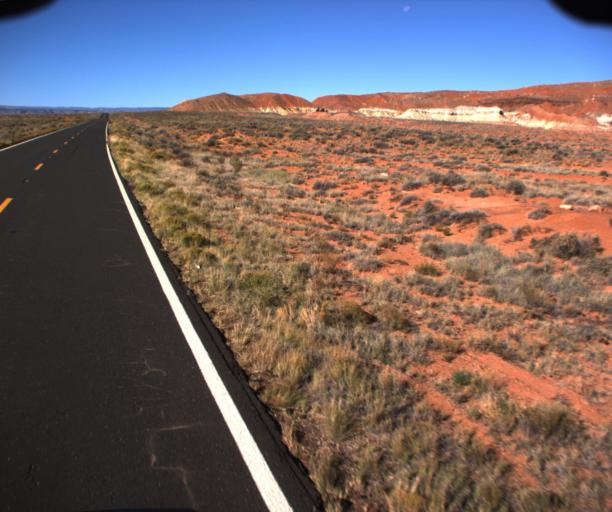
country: US
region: Arizona
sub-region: Coconino County
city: LeChee
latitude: 36.6877
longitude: -111.8256
